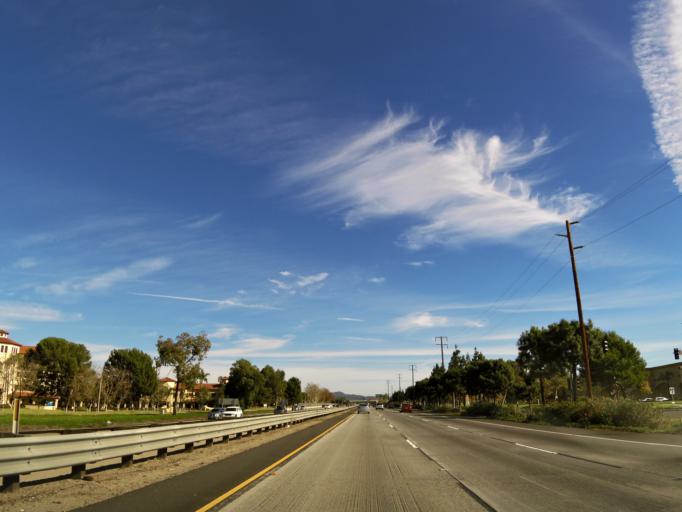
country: US
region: California
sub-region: Ventura County
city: Camarillo
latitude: 34.2184
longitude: -119.0606
